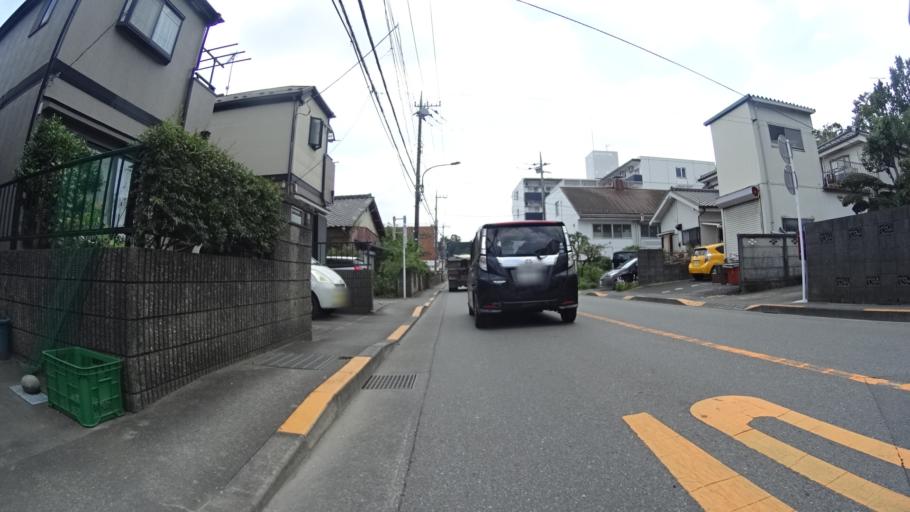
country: JP
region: Tokyo
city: Fussa
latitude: 35.7446
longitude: 139.3197
